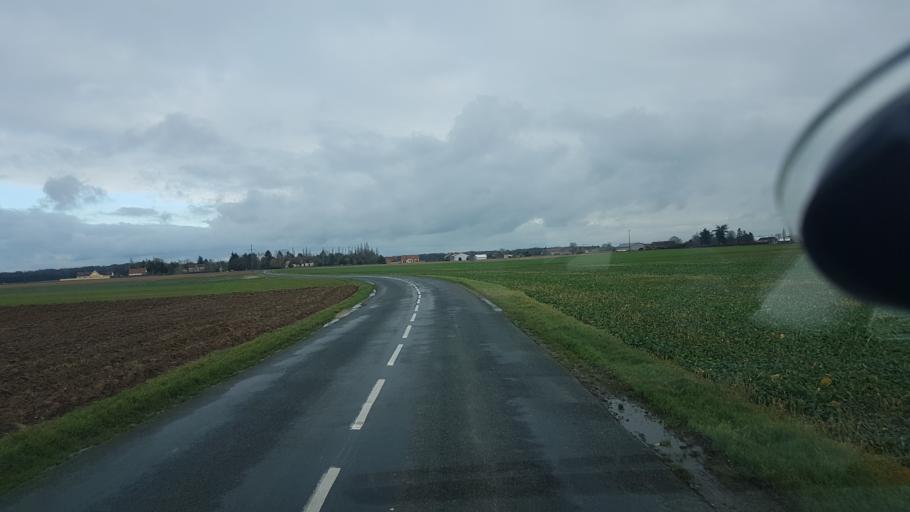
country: FR
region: Ile-de-France
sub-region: Departement de Seine-et-Marne
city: Souppes-sur-Loing
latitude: 48.2155
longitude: 2.7924
